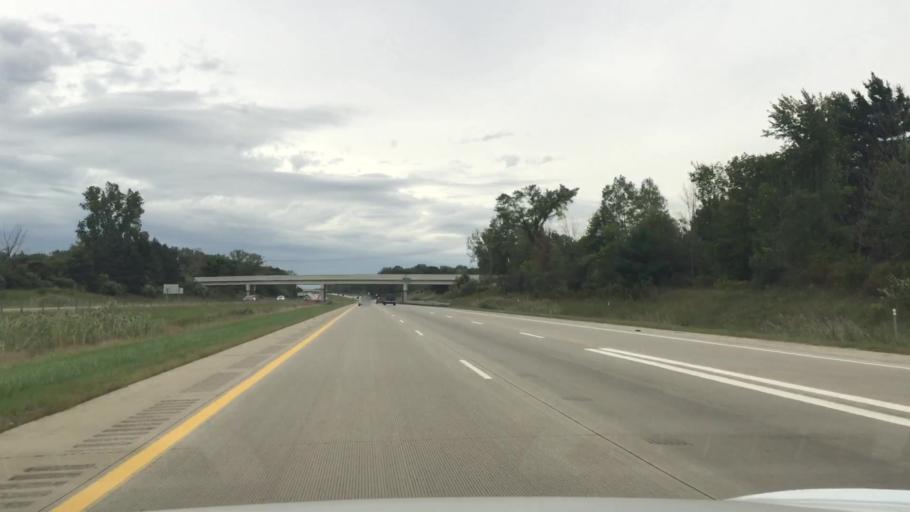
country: US
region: Michigan
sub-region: Macomb County
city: Richmond
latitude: 42.8105
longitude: -82.6325
